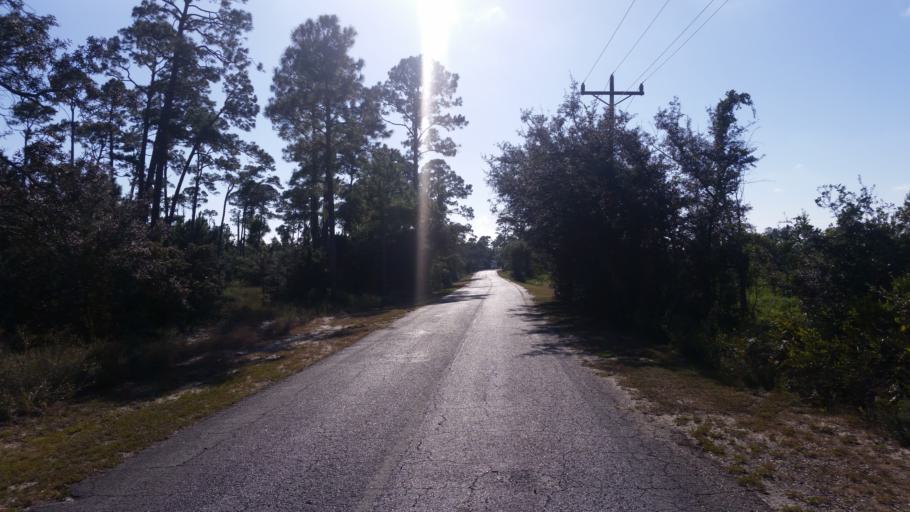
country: US
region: Alabama
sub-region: Baldwin County
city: Orange Beach
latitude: 30.2724
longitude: -87.6239
